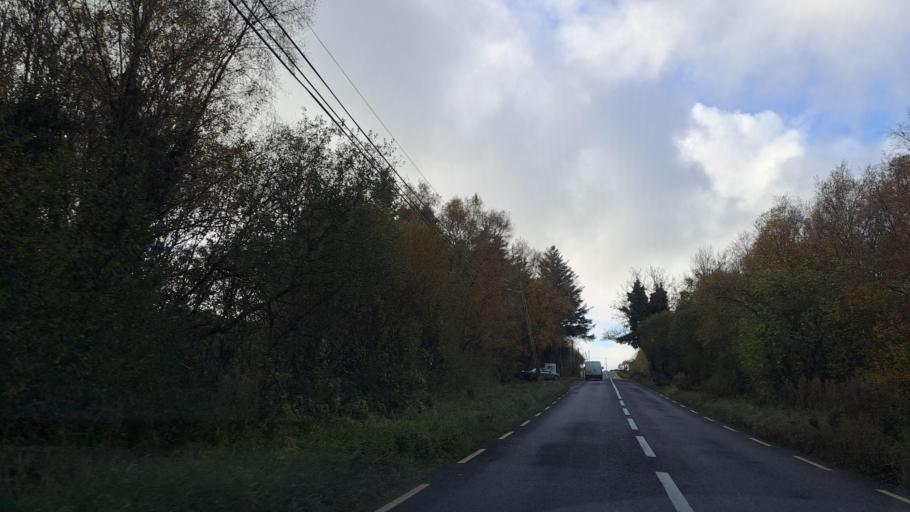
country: IE
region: Ulster
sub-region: An Cabhan
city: Virginia
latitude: 53.8491
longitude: -7.0612
